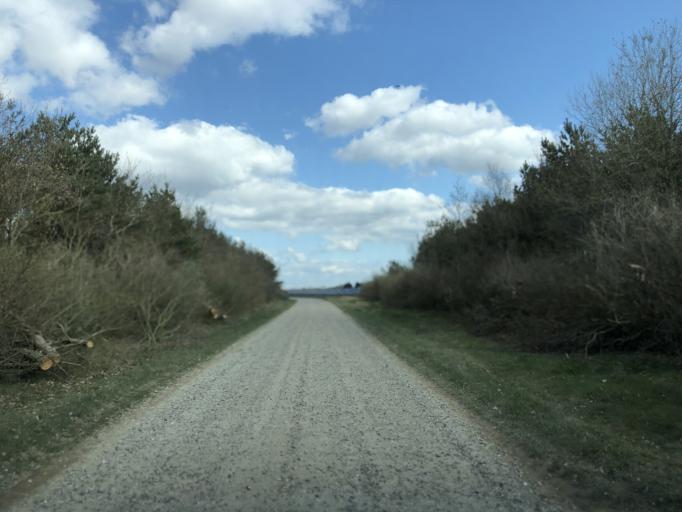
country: DK
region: Central Jutland
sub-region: Holstebro Kommune
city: Ulfborg
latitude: 56.3895
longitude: 8.2134
